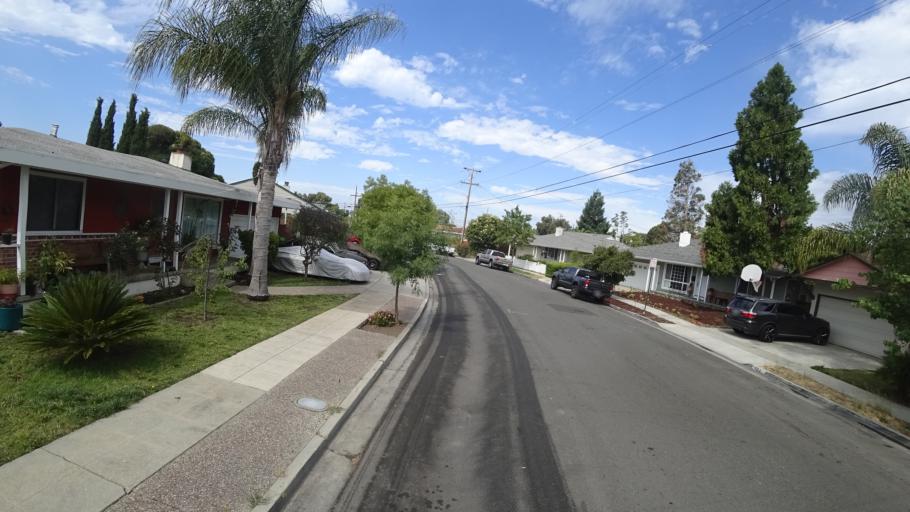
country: US
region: California
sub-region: Alameda County
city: Hayward
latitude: 37.6457
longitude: -122.0742
